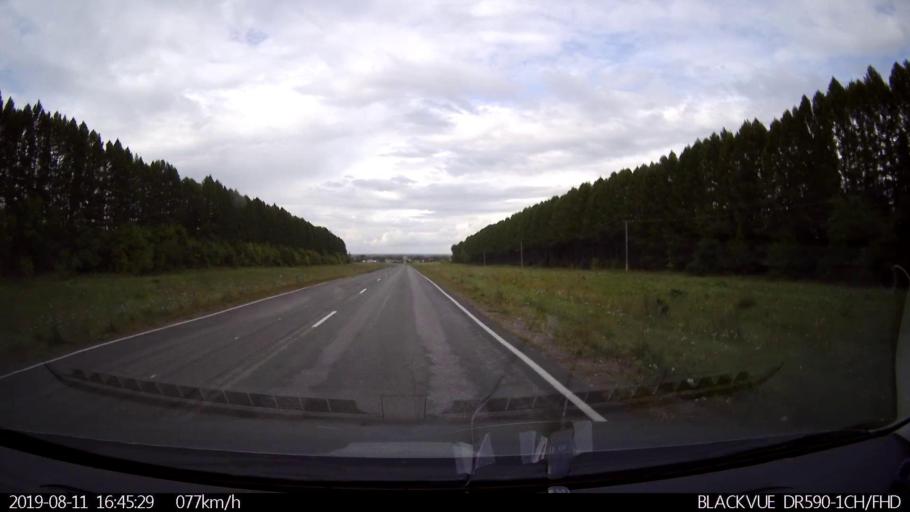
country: RU
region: Ulyanovsk
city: Mayna
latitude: 54.1901
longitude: 47.6862
